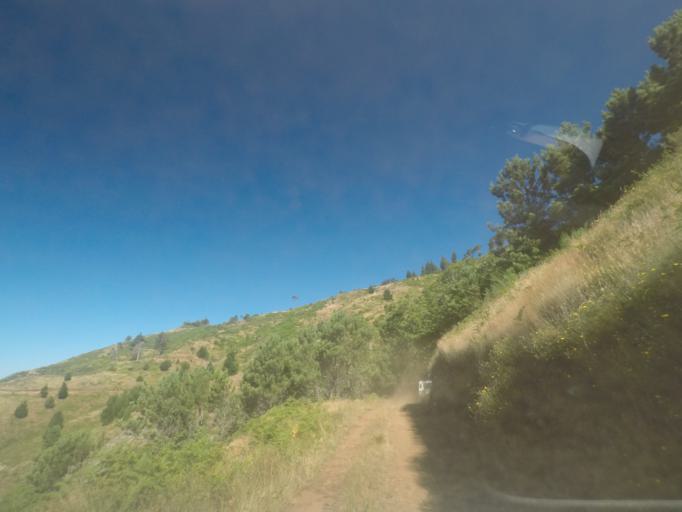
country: PT
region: Madeira
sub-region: Funchal
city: Nossa Senhora do Monte
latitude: 32.7042
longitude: -16.9081
